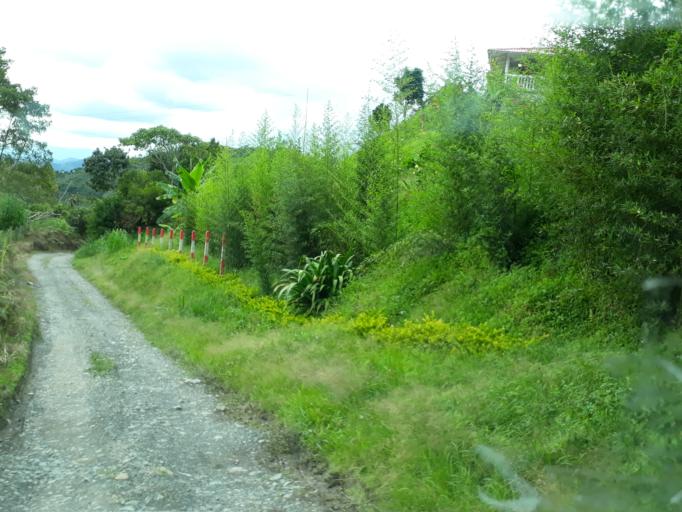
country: CO
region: Cundinamarca
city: Pacho
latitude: 5.1599
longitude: -74.2369
